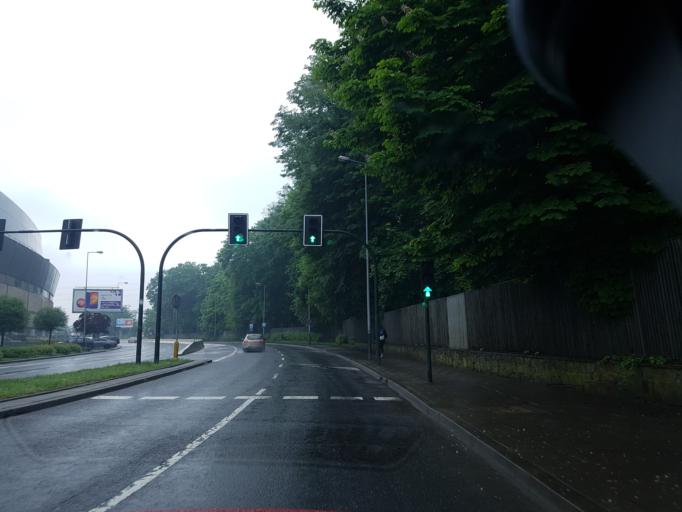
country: PL
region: Lesser Poland Voivodeship
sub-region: Krakow
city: Krakow
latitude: 50.0540
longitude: 19.9536
